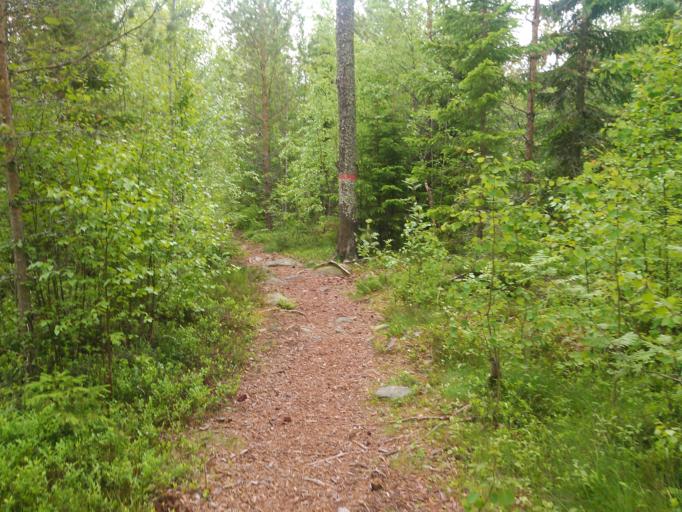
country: SE
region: Vaesterbotten
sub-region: Umea Kommun
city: Ersmark
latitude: 63.7978
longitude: 20.3497
